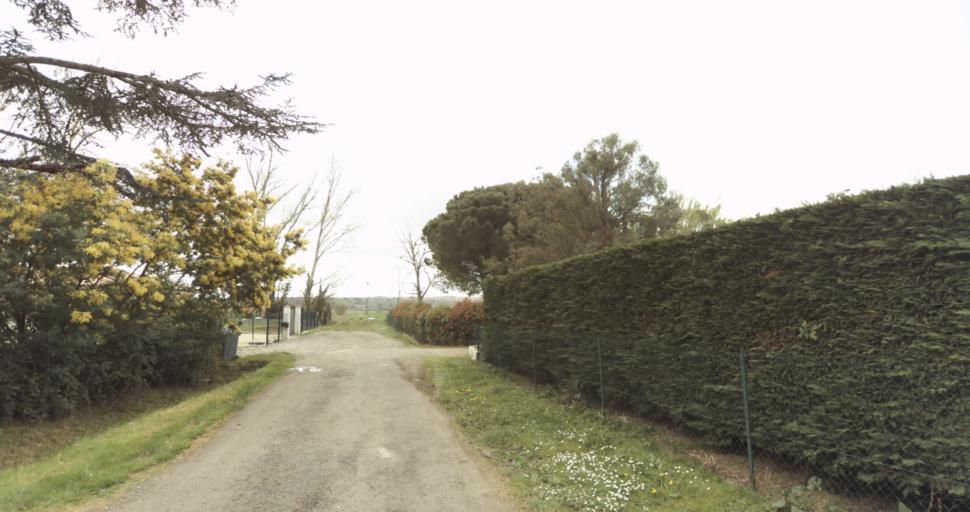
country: FR
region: Midi-Pyrenees
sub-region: Departement de la Haute-Garonne
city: Auterive
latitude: 43.3259
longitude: 1.4699
